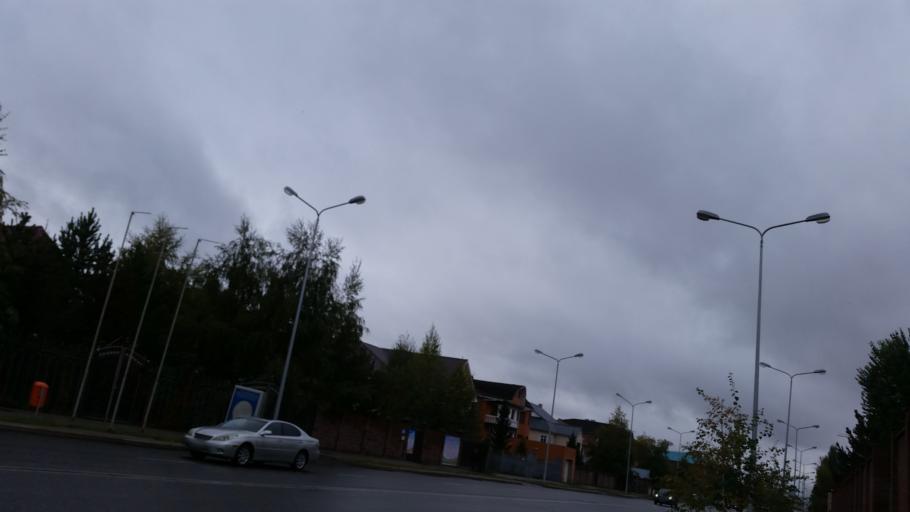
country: KZ
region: Astana Qalasy
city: Astana
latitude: 51.1500
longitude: 71.4917
